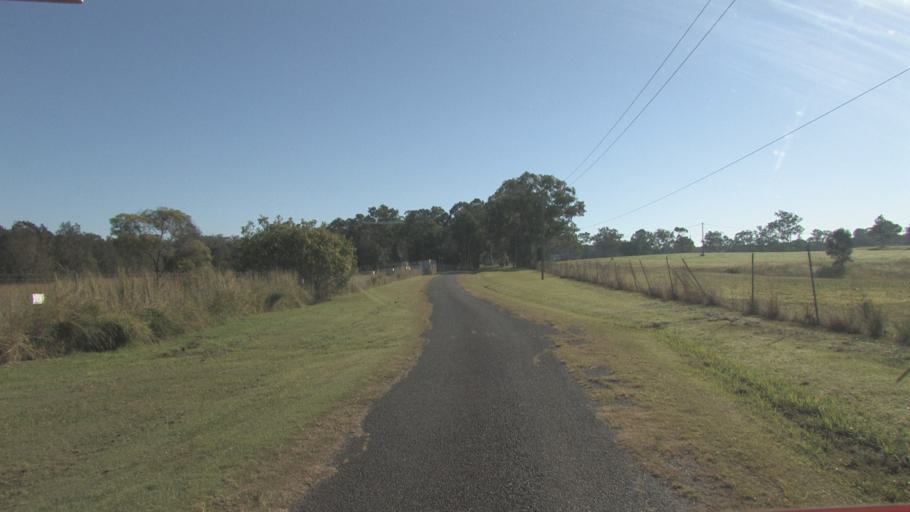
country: AU
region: Queensland
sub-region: Gold Coast
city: Yatala
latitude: -27.6929
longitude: 153.2796
